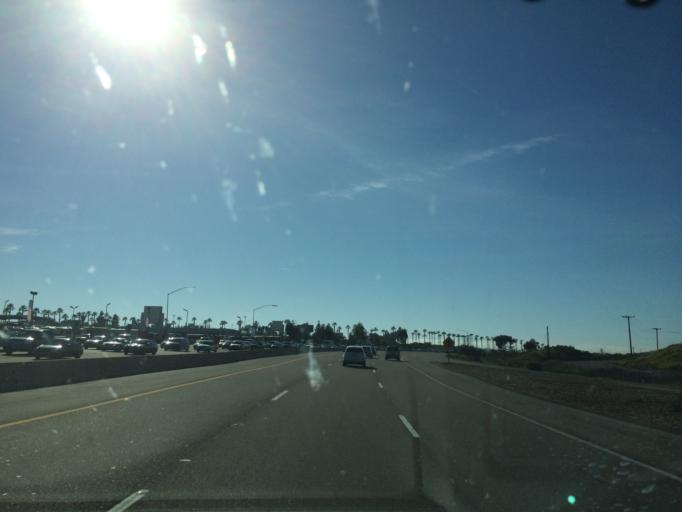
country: US
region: California
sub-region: San Diego County
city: La Jolla
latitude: 32.8376
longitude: -117.1539
